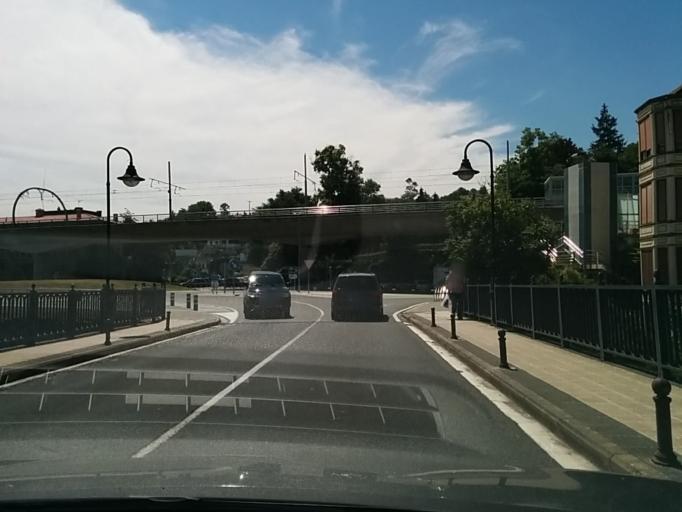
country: ES
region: Basque Country
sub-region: Provincia de Guipuzcoa
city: Orio
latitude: 43.2748
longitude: -2.1256
